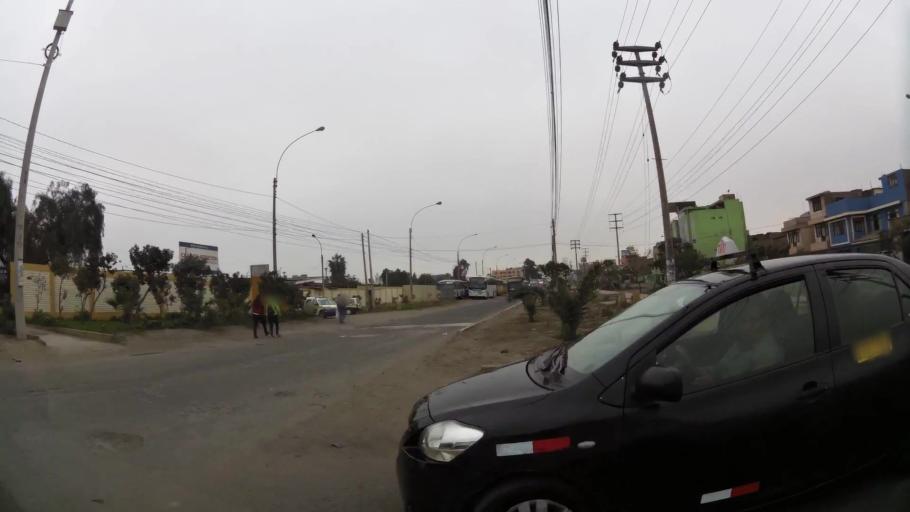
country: PE
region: Lima
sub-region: Lima
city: Surco
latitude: -12.1719
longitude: -76.9769
